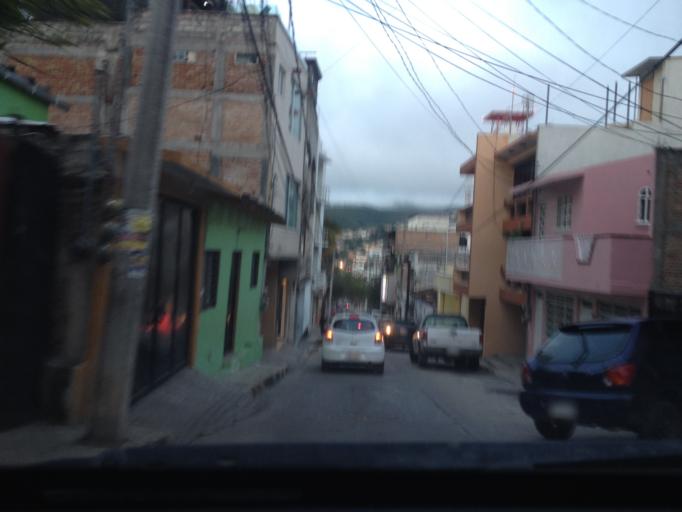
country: MX
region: Guerrero
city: Chilpancingo de los Bravos
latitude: 17.5569
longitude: -99.5011
